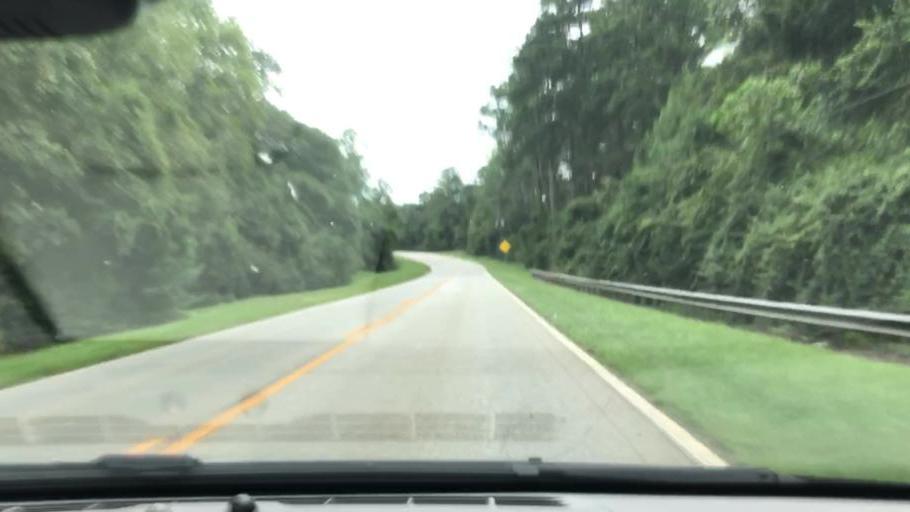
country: US
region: Georgia
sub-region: Early County
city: Blakely
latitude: 31.4044
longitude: -84.9301
